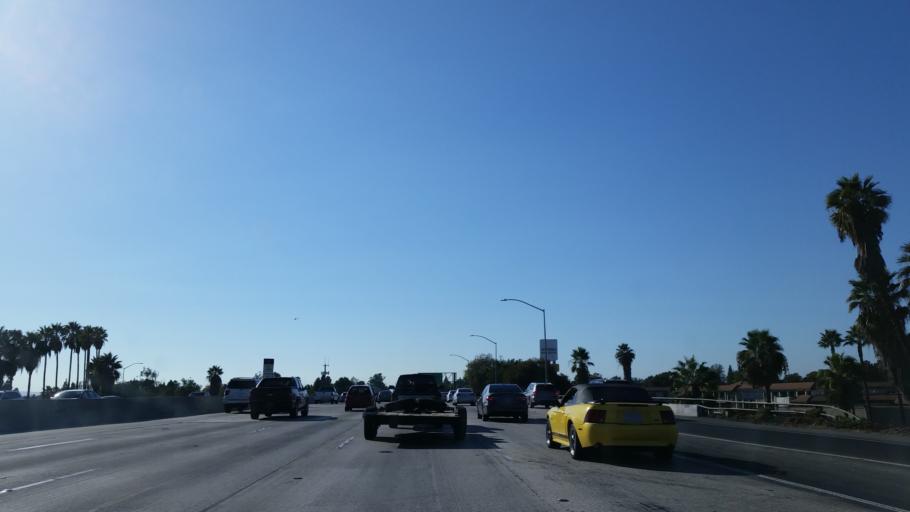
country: US
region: California
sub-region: Los Angeles County
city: Artesia
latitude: 33.8765
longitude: -118.0817
